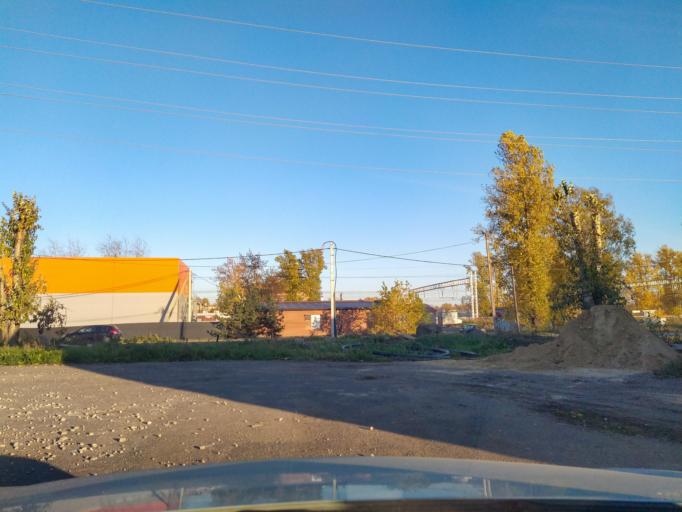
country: RU
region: Leningrad
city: Siverskiy
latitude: 59.3556
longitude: 30.0608
